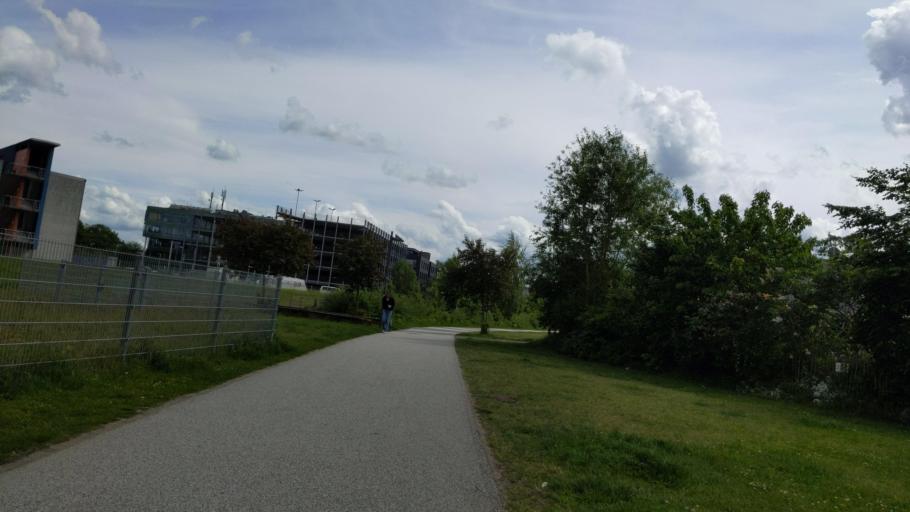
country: DE
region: Schleswig-Holstein
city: Luebeck
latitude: 53.8363
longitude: 10.6947
